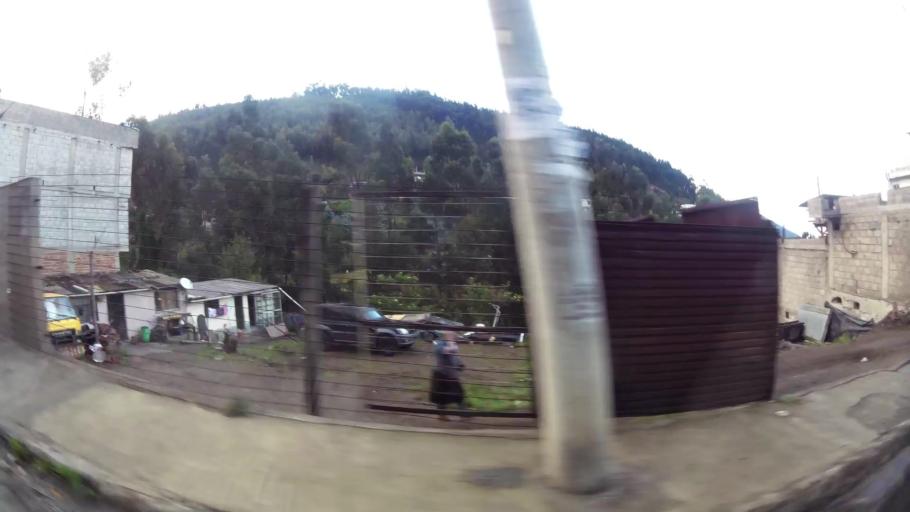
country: EC
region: Pichincha
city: Quito
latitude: -0.1188
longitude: -78.5143
